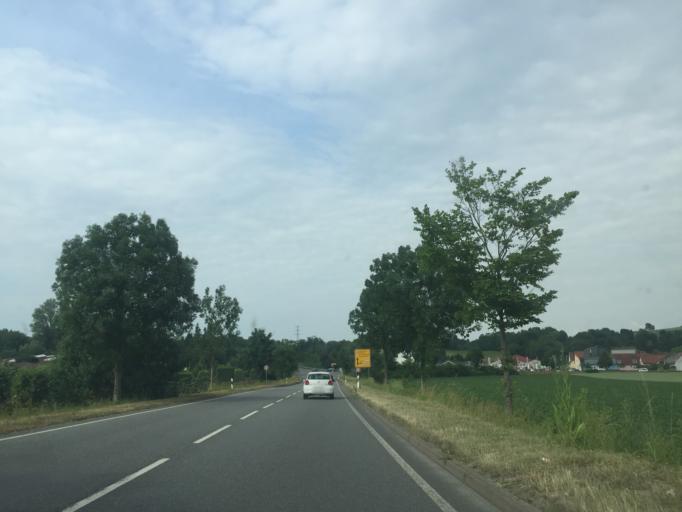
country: DE
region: Baden-Wuerttemberg
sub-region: Karlsruhe Region
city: Mauer
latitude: 49.3447
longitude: 8.7914
